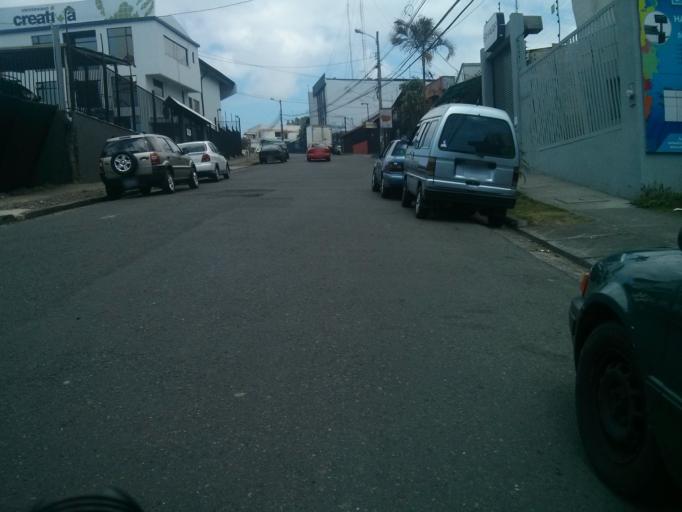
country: CR
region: San Jose
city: San Pedro
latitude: 9.9270
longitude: -84.0545
